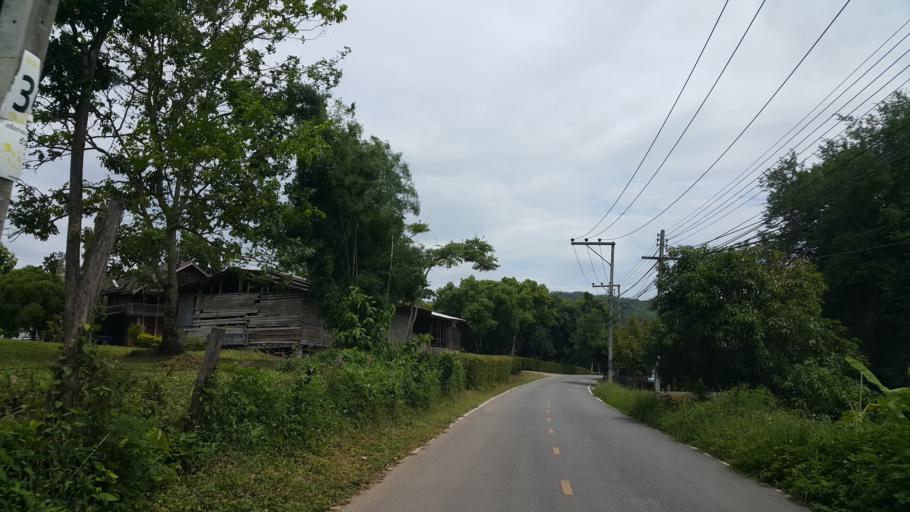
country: TH
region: Lampang
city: Mueang Pan
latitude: 18.7789
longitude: 99.5241
